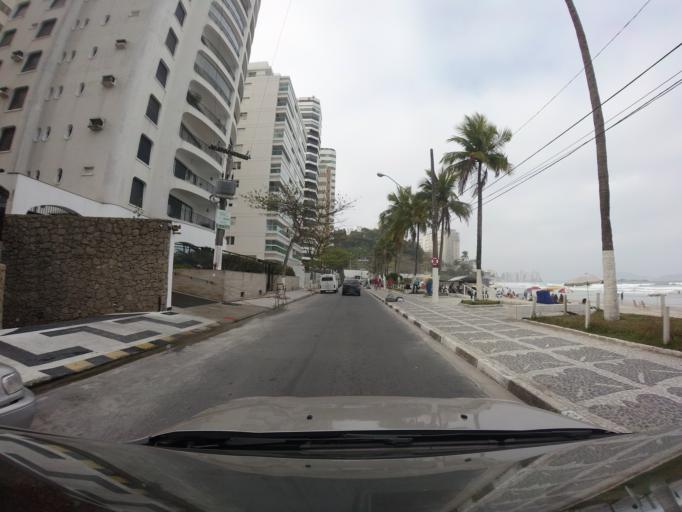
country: BR
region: Sao Paulo
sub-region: Guaruja
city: Guaruja
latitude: -24.0051
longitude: -46.2679
